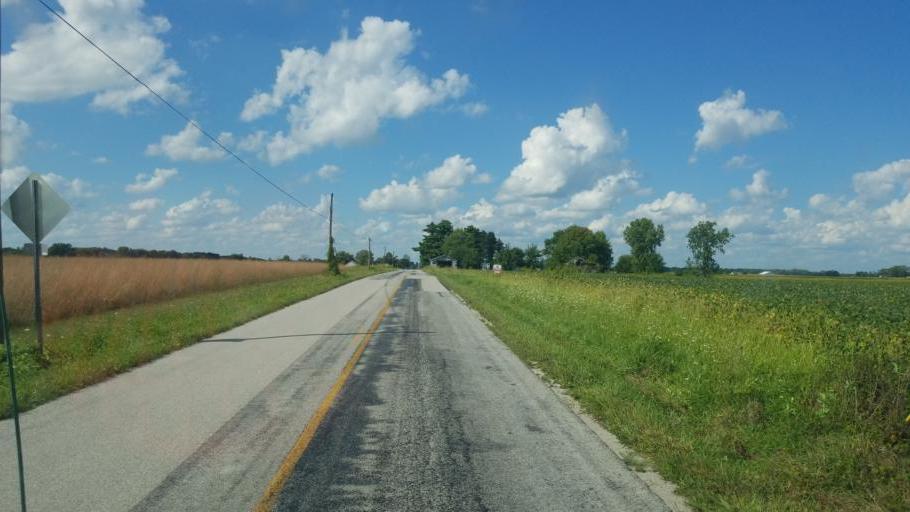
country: US
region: Ohio
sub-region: Union County
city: Richwood
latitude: 40.5143
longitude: -83.3836
